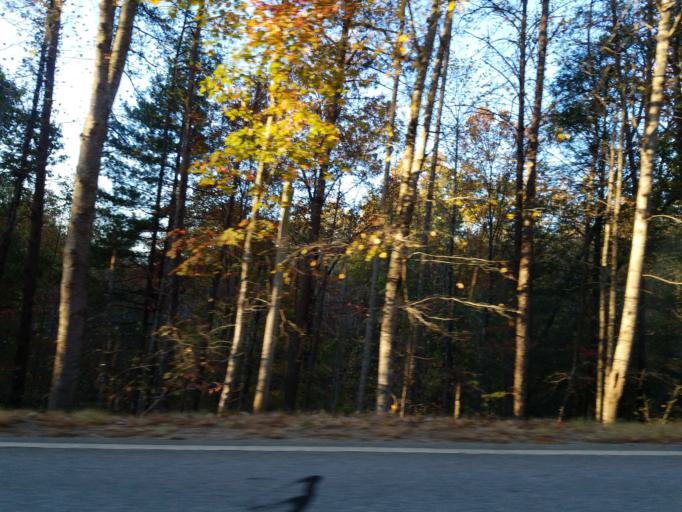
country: US
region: Georgia
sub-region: Dawson County
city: Dawsonville
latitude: 34.5472
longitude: -84.1168
